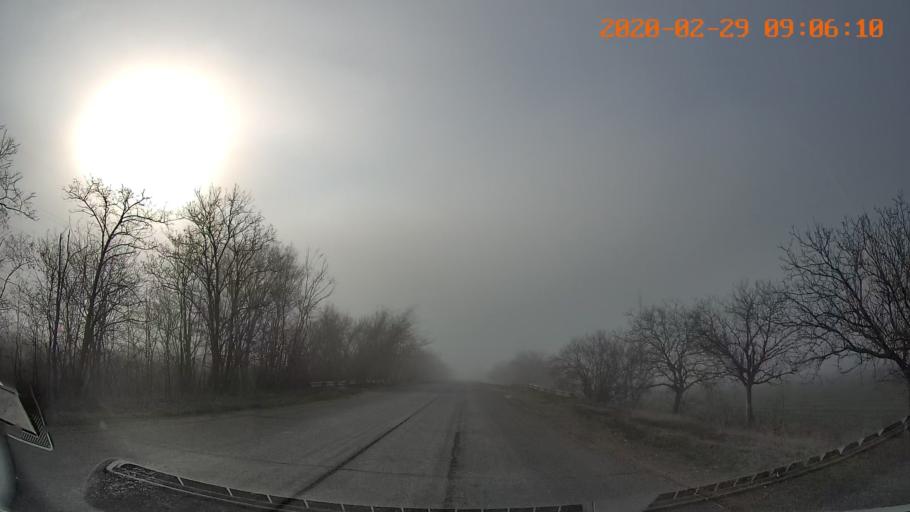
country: MD
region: Telenesti
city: Tiraspolul Nou
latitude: 46.8792
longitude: 29.7434
